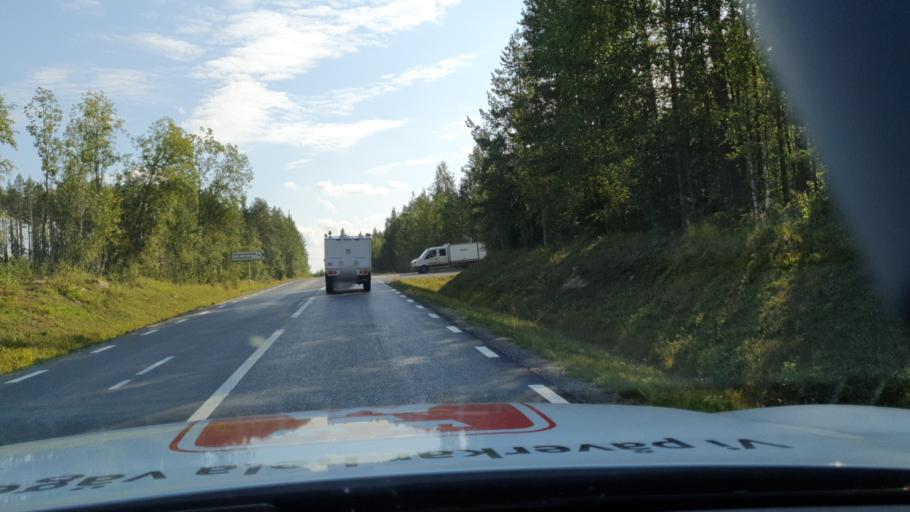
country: SE
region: Vaesterbotten
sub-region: Dorotea Kommun
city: Dorotea
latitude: 64.0963
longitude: 16.0860
